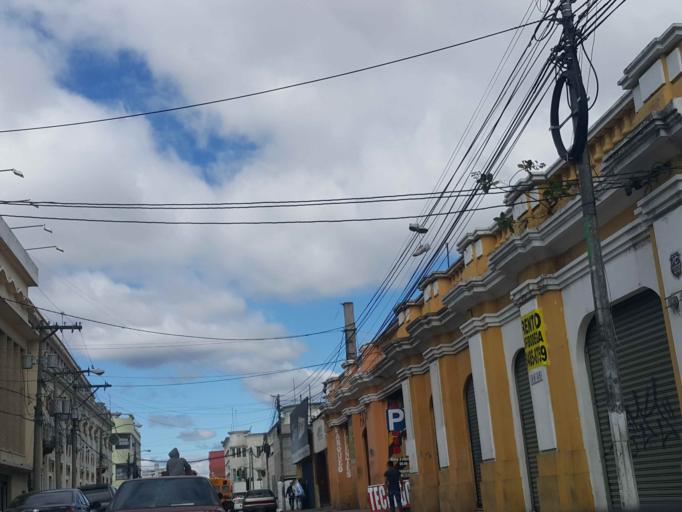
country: GT
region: Guatemala
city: Guatemala City
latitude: 14.6297
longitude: -90.5141
